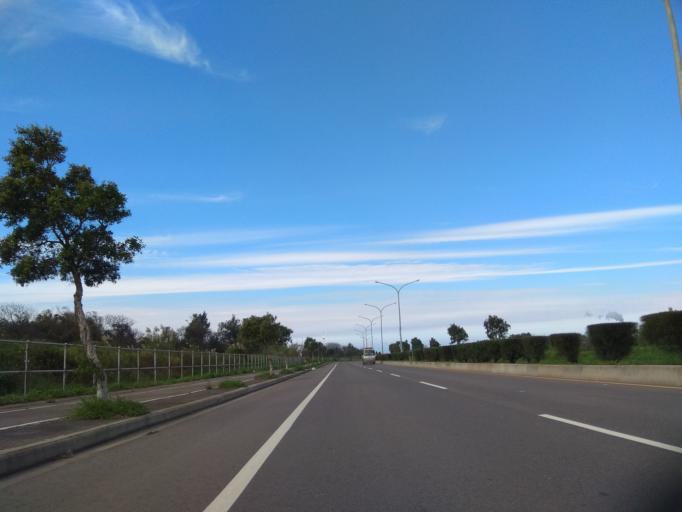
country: TW
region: Taiwan
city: Taoyuan City
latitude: 25.0670
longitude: 121.1748
